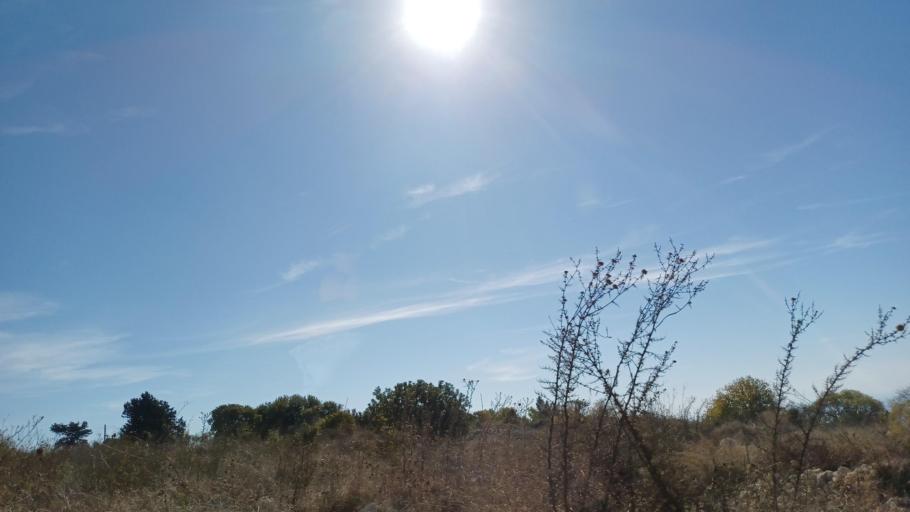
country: CY
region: Pafos
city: Pegeia
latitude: 34.9434
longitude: 32.4040
